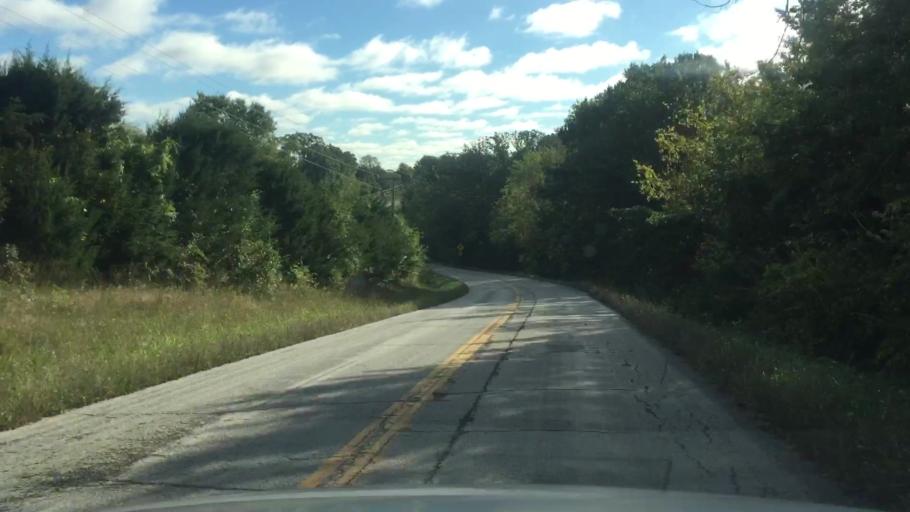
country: US
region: Missouri
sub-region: Howard County
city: Fayette
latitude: 39.1053
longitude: -92.7664
